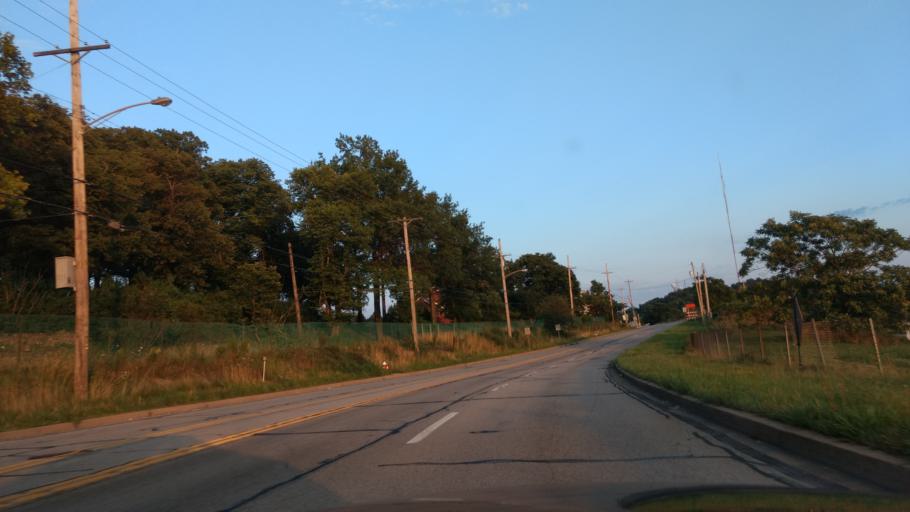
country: US
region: Pennsylvania
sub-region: Allegheny County
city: West View
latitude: 40.5029
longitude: -80.0245
